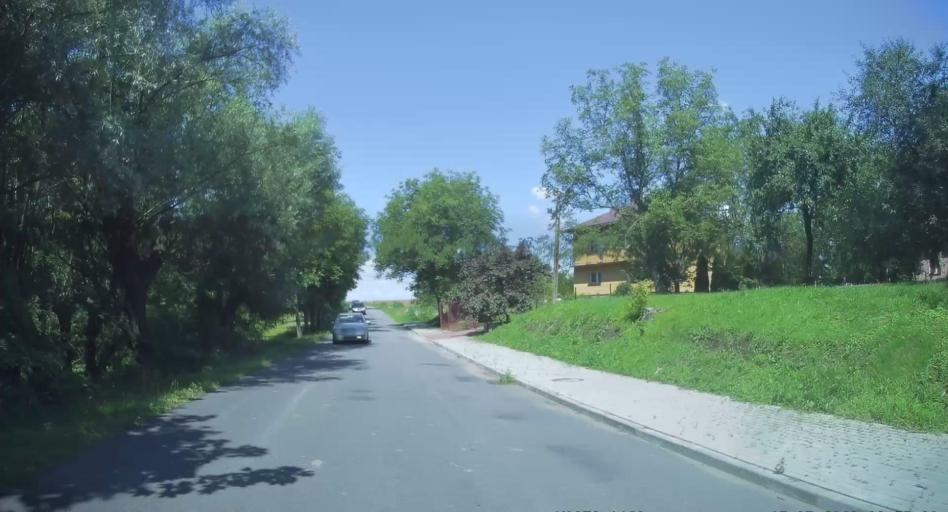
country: PL
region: Subcarpathian Voivodeship
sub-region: Powiat jaroslawski
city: Sosnica
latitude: 49.8657
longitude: 22.8707
